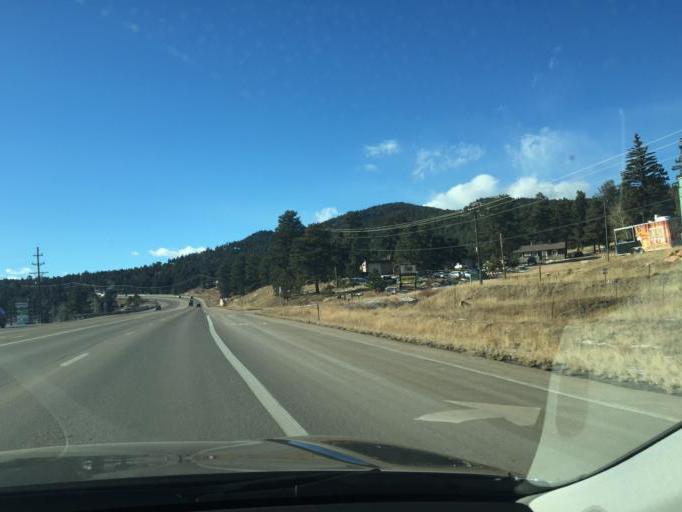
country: US
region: Colorado
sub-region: Jefferson County
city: Evergreen
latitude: 39.5018
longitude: -105.3240
